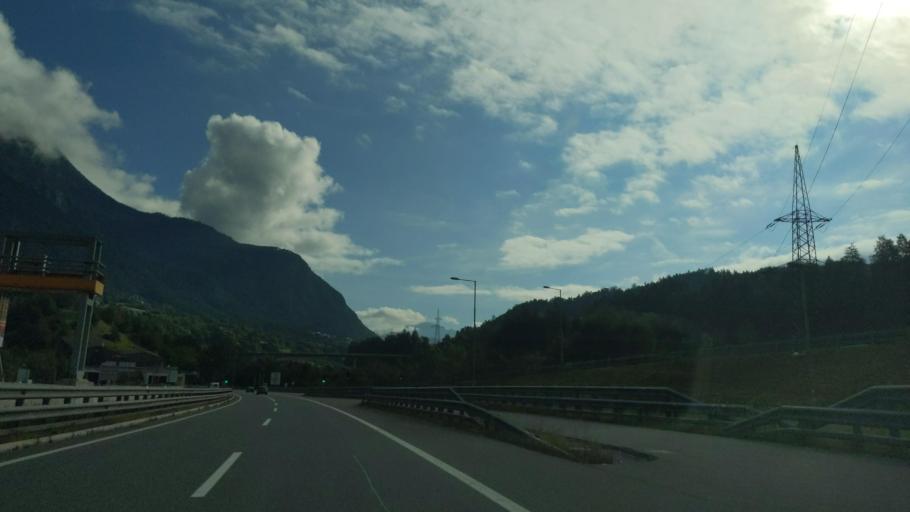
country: AT
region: Tyrol
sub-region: Politischer Bezirk Imst
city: Karrosten
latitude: 47.2173
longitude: 10.7486
